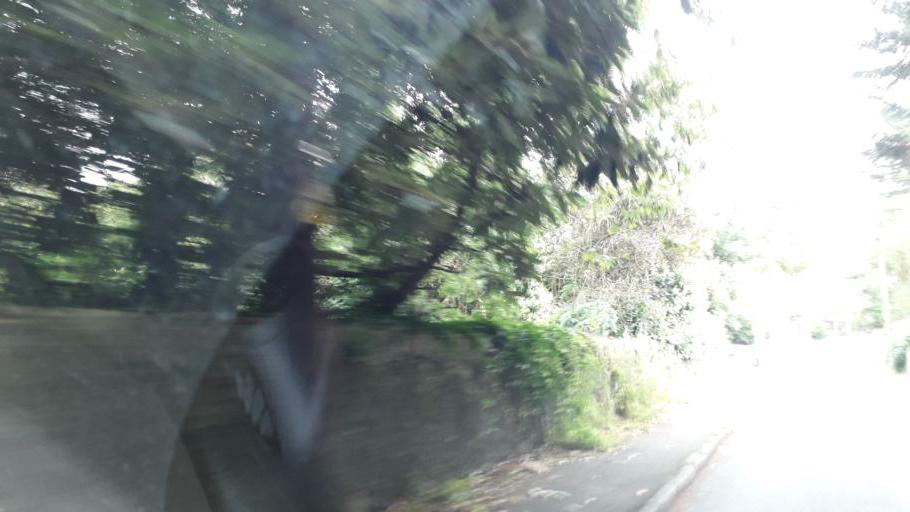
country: IE
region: Leinster
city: Cabinteely
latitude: 53.2552
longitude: -6.1612
